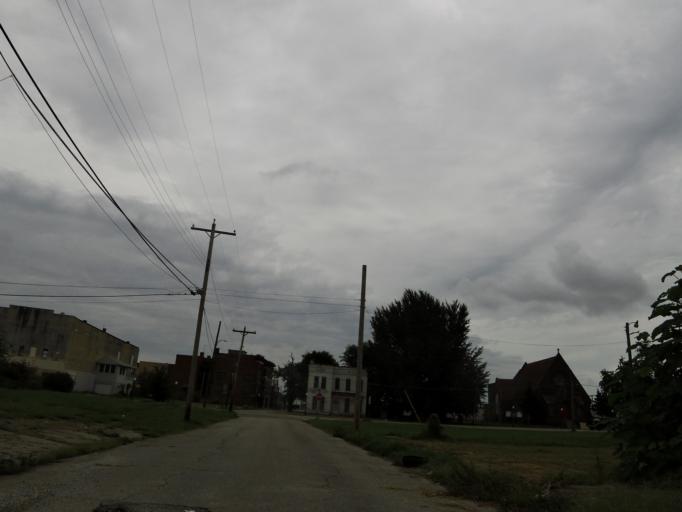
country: US
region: Illinois
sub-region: Alexander County
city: Cairo
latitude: 36.9989
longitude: -89.1673
